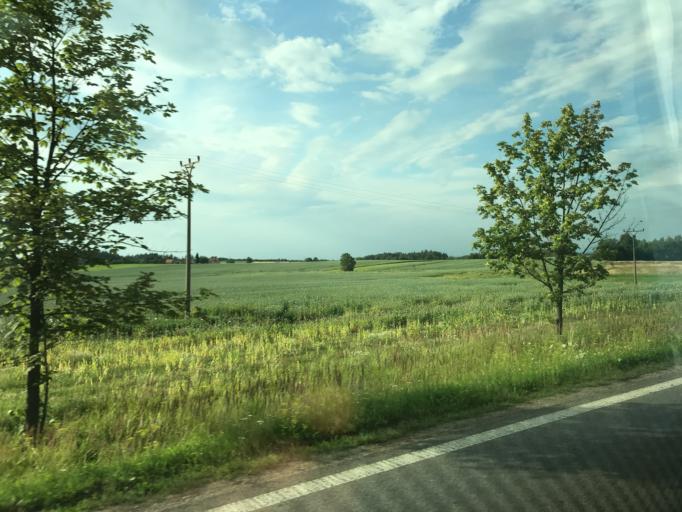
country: CZ
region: Jihocesky
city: Lisov
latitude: 49.0105
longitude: 14.5915
